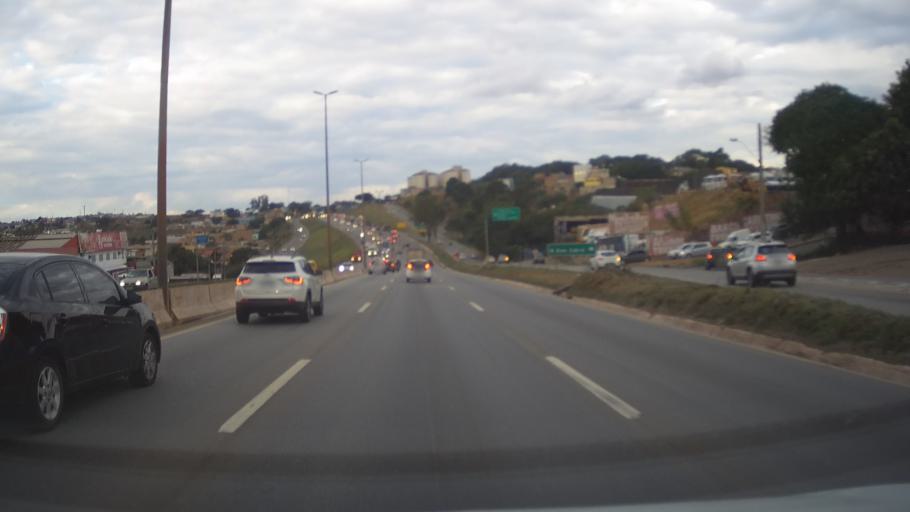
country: BR
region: Minas Gerais
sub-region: Contagem
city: Contagem
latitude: -19.9198
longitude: -43.9991
